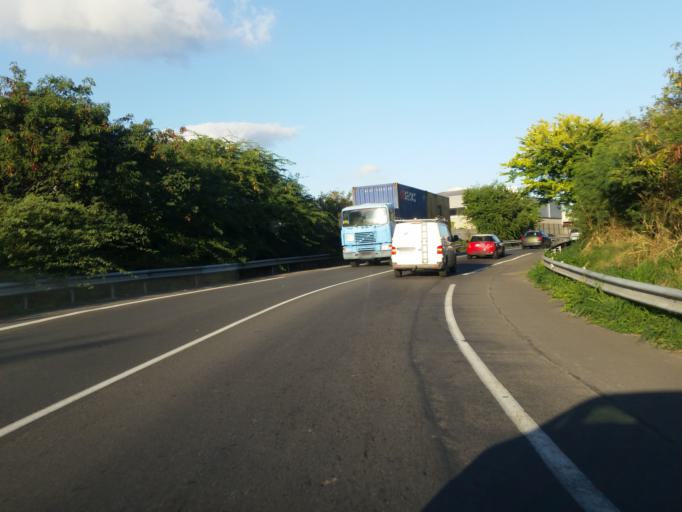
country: RE
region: Reunion
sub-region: Reunion
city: La Possession
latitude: -20.9351
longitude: 55.3284
